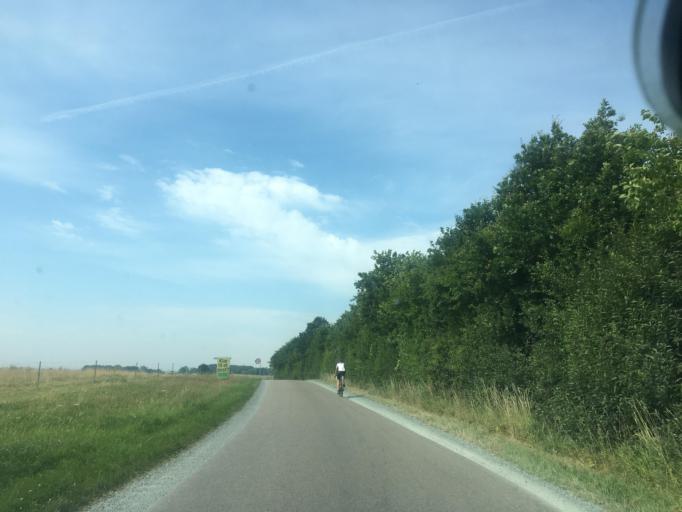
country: DK
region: Zealand
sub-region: Faxe Kommune
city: Fakse
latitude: 55.1856
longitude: 12.1082
